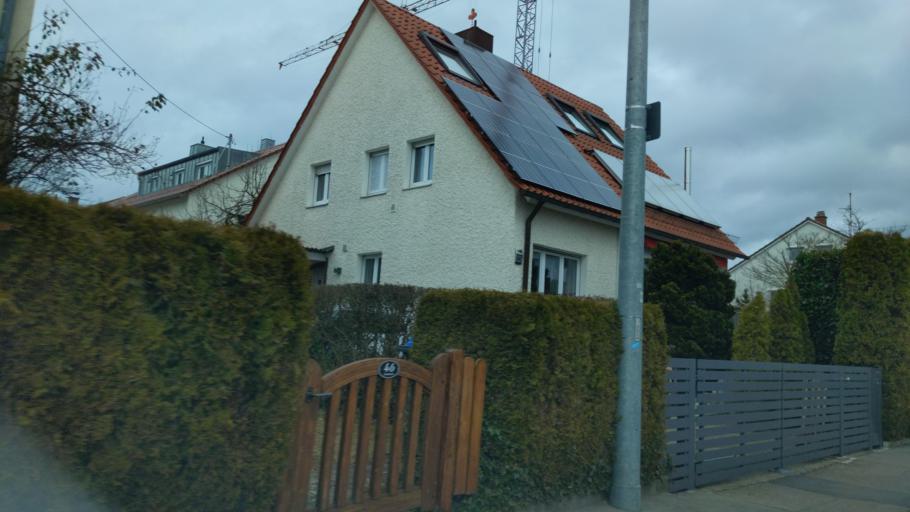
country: DE
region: Baden-Wuerttemberg
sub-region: Regierungsbezirk Stuttgart
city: Ostfildern
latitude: 48.7291
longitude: 9.2465
